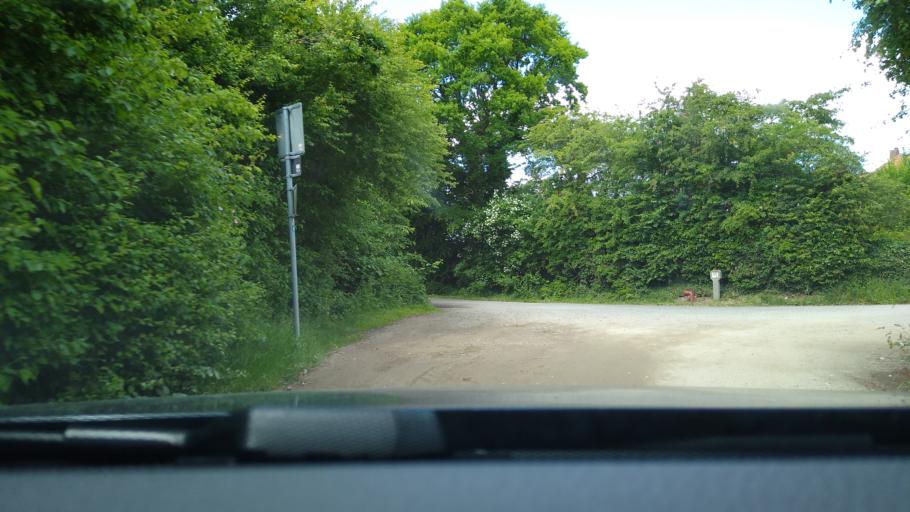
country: DE
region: Schleswig-Holstein
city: Dahme
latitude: 54.2011
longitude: 11.0912
